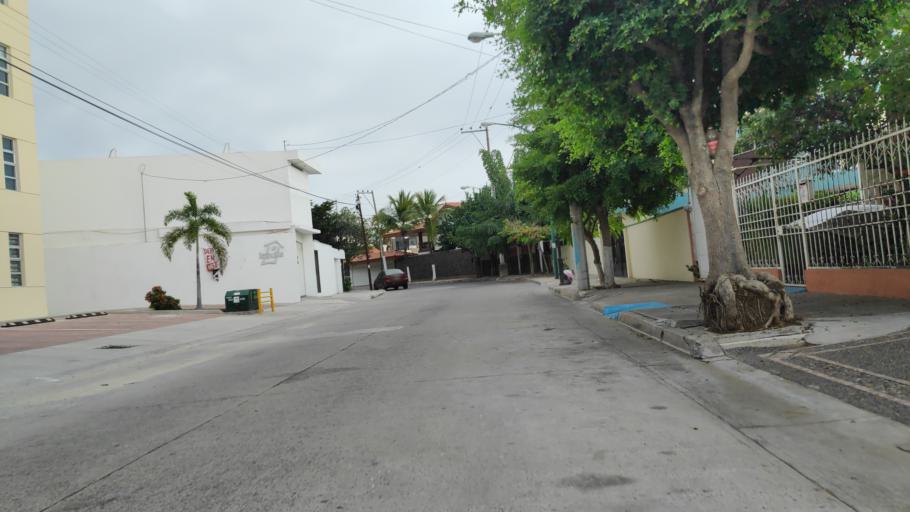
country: MX
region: Sinaloa
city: Culiacan
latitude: 24.7941
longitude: -107.3971
